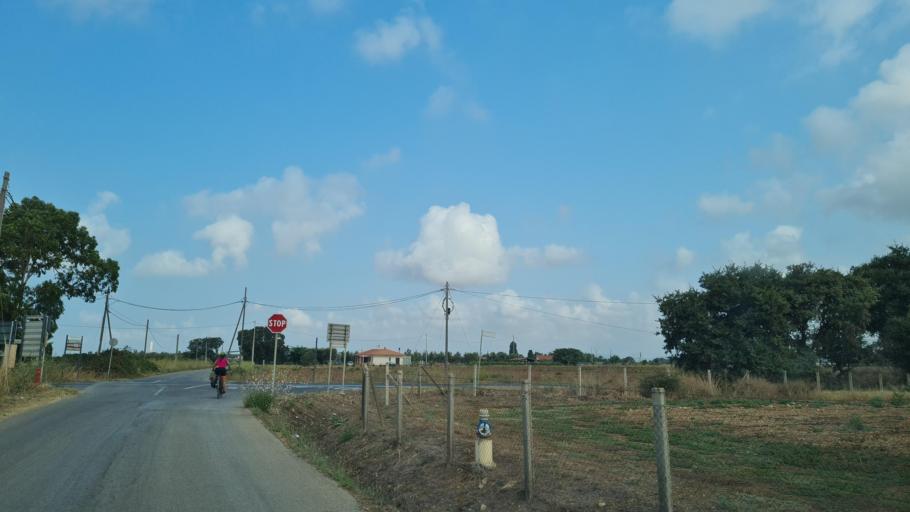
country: IT
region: Latium
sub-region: Provincia di Viterbo
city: Montalto di Castro
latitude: 42.3157
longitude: 11.6092
